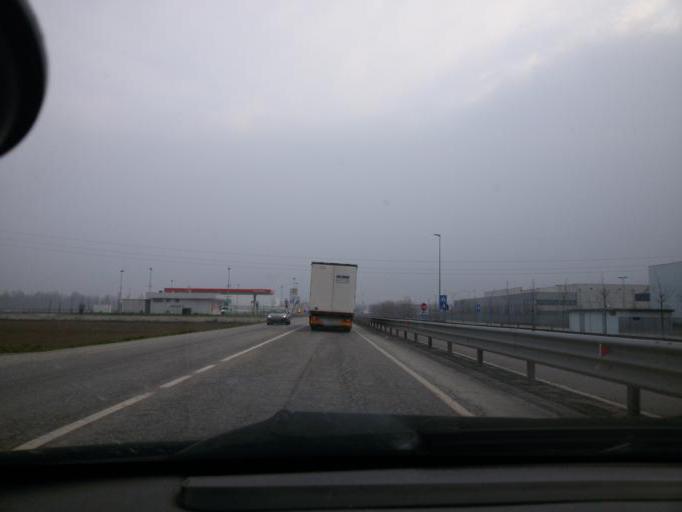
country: IT
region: Piedmont
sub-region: Provincia di Vercelli
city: Vercelli
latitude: 45.2993
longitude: 8.3912
